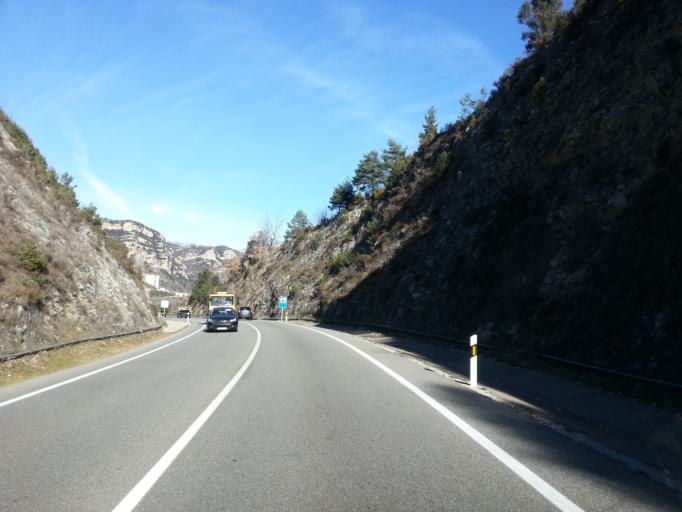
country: ES
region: Catalonia
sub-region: Provincia de Barcelona
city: Berga
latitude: 42.1573
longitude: 1.8590
